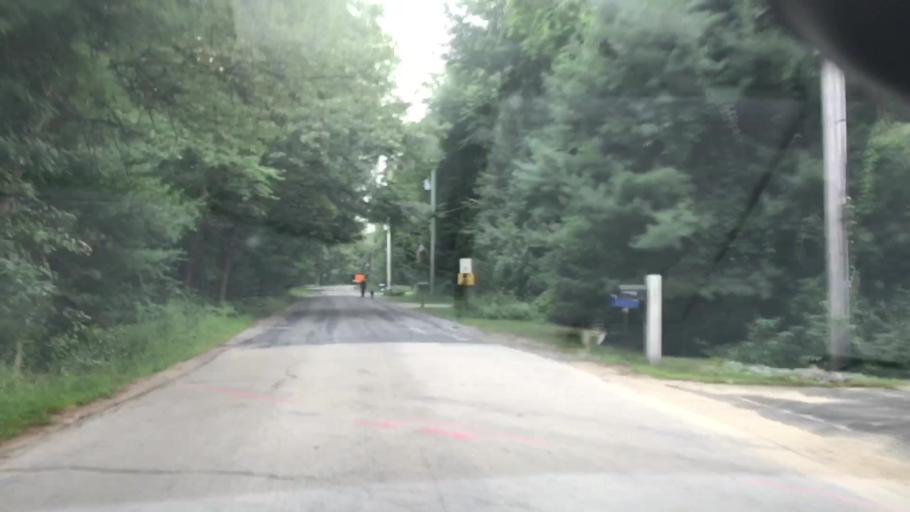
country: US
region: New Hampshire
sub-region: Hillsborough County
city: Bedford
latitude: 42.9365
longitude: -71.4742
